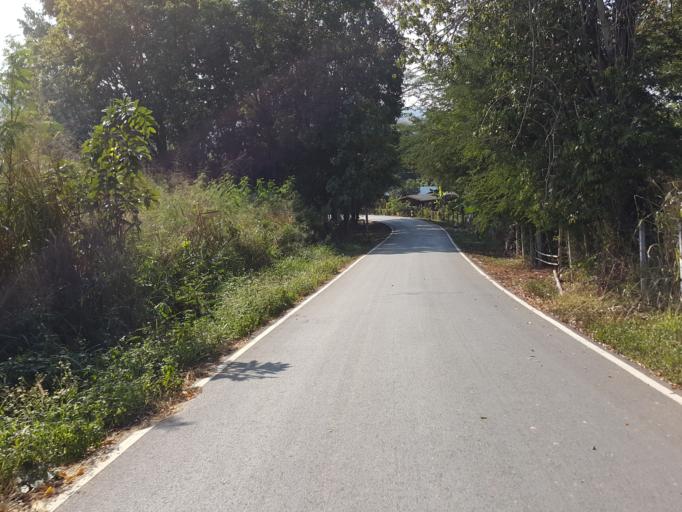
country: TH
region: Chiang Mai
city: Mae On
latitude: 18.8244
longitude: 99.2303
